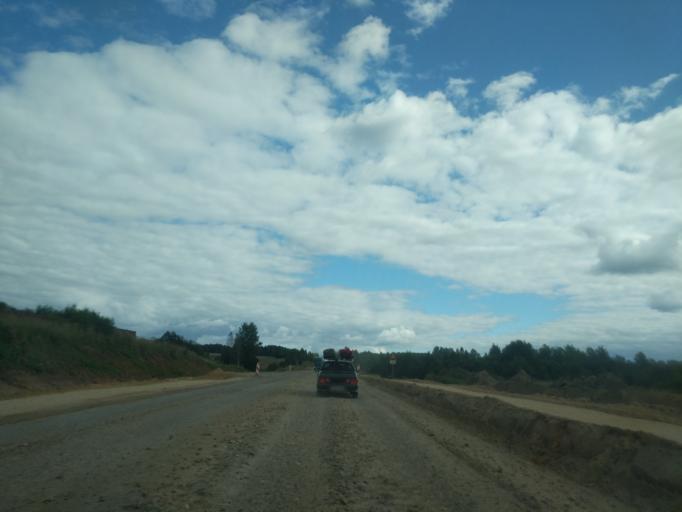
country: RU
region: Kostroma
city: Sudislavl'
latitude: 57.8738
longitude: 41.7375
